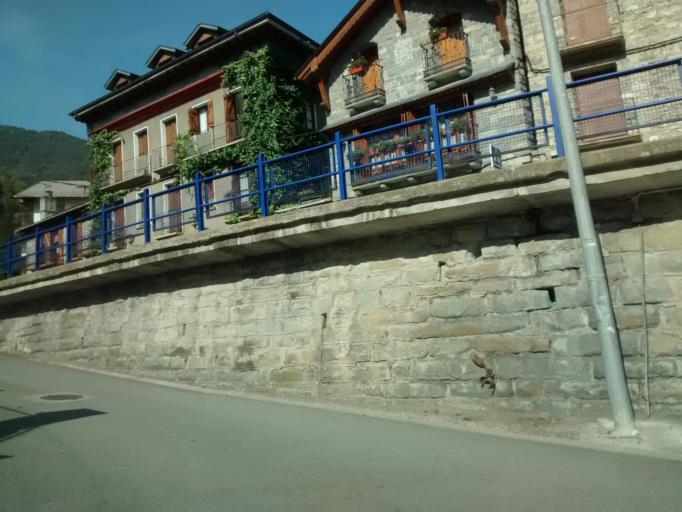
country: ES
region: Aragon
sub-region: Provincia de Huesca
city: Broto
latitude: 42.6047
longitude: -0.1236
